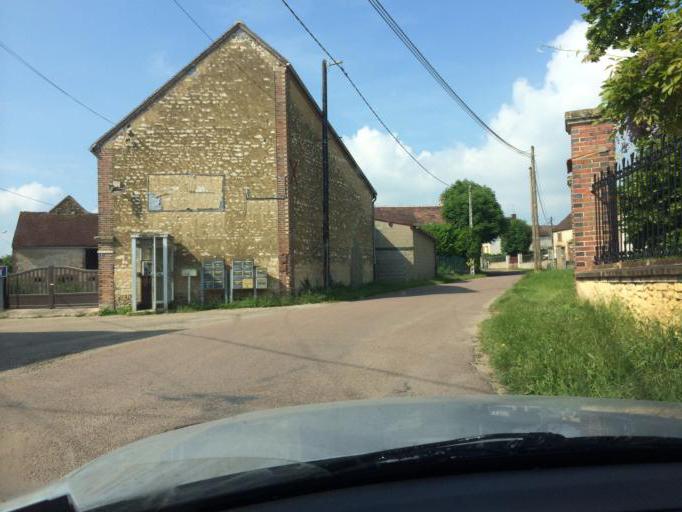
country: FR
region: Bourgogne
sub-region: Departement de l'Yonne
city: Aillant-sur-Tholon
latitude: 47.8681
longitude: 3.3970
